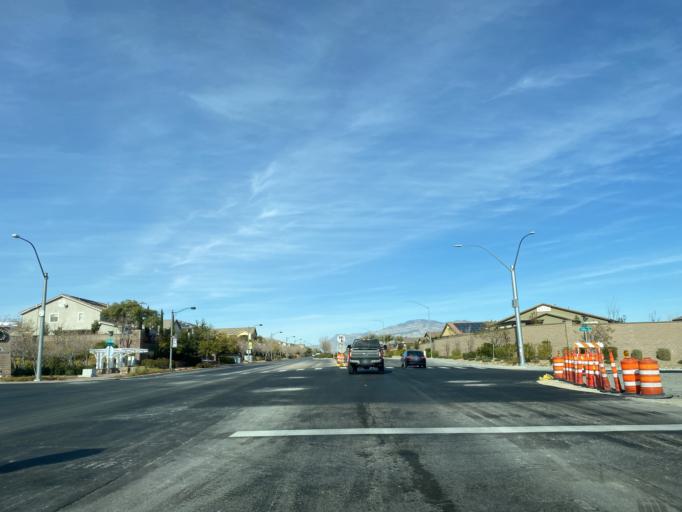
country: US
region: Nevada
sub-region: Clark County
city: Summerlin South
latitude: 36.2919
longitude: -115.3149
